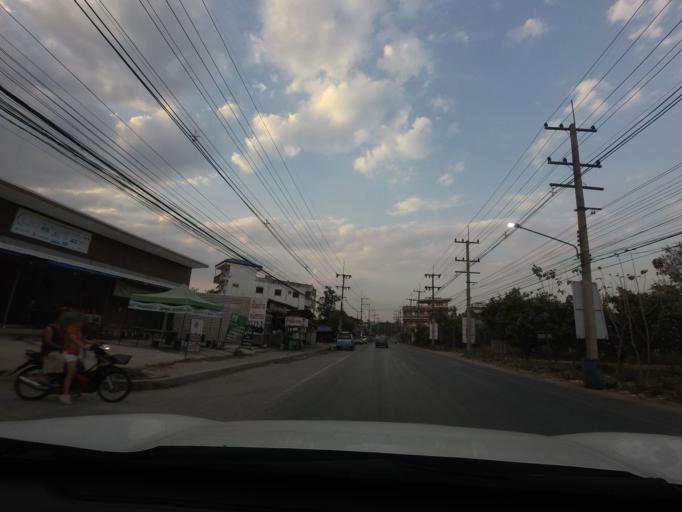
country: TH
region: Nakhon Ratchasima
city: Pak Chong
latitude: 14.7137
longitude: 101.4381
